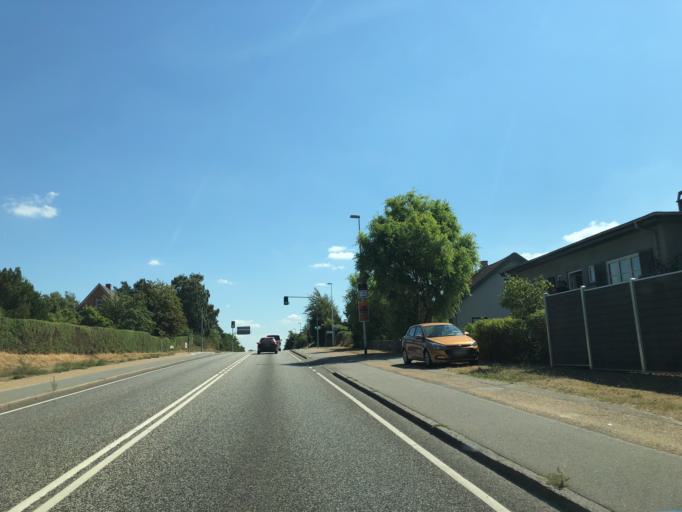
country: DK
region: Capital Region
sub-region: Halsnaes Kommune
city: Hundested
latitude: 55.9627
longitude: 11.8601
